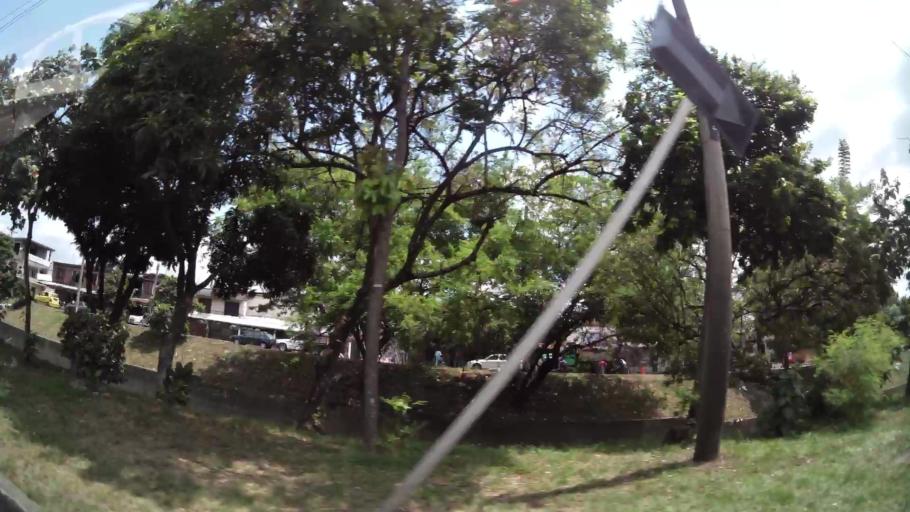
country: CO
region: Valle del Cauca
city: Cali
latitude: 3.4574
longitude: -76.4817
